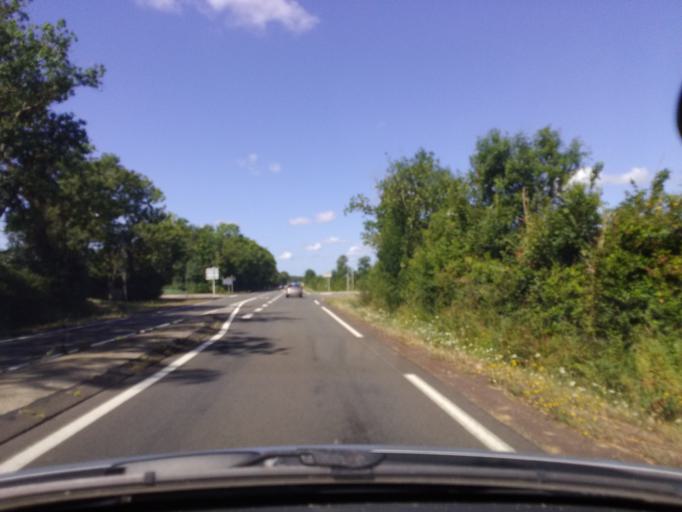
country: FR
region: Pays de la Loire
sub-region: Departement de la Vendee
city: Moutiers-les-Mauxfaits
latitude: 46.4553
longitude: -1.3913
